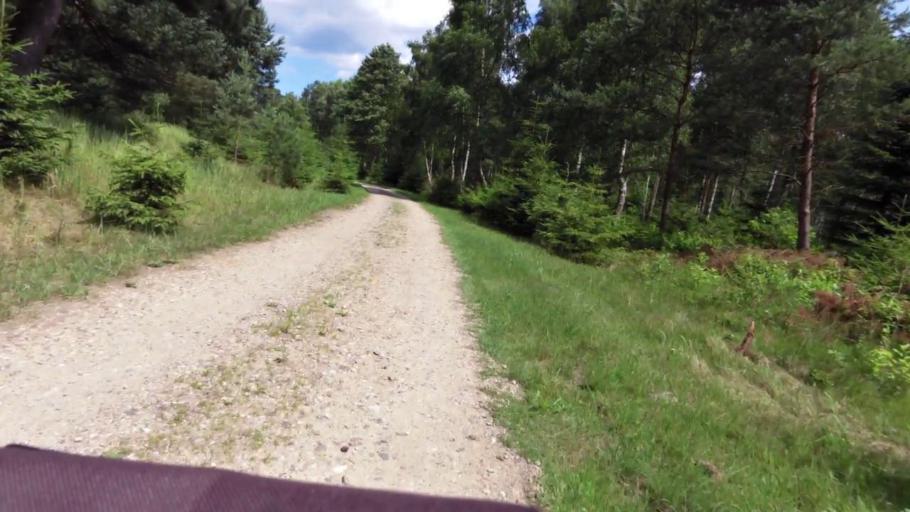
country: PL
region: West Pomeranian Voivodeship
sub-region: Powiat gryficki
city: Mrzezyno
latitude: 54.1278
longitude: 15.2482
